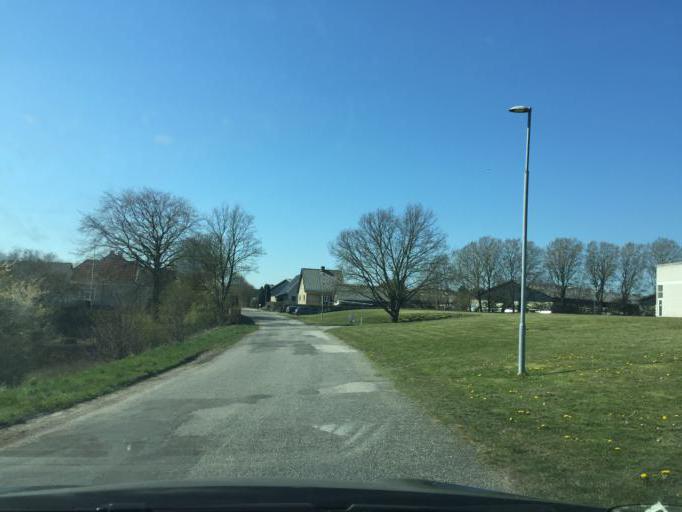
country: DK
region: South Denmark
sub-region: Faaborg-Midtfyn Kommune
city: Ringe
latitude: 55.2451
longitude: 10.4896
